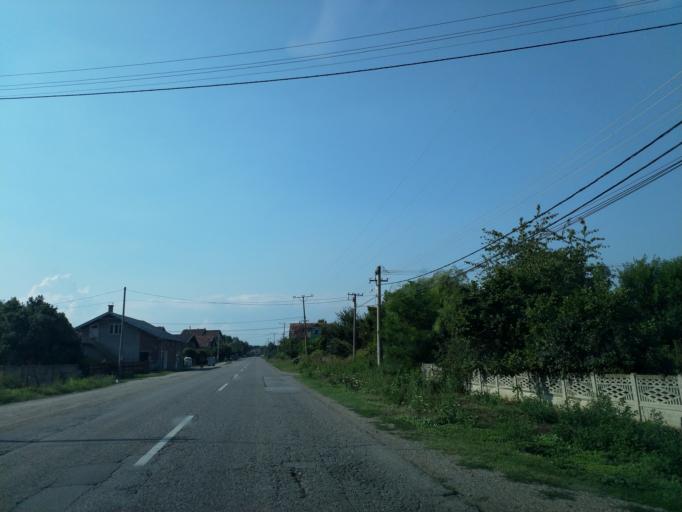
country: RS
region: Central Serbia
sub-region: Rasinski Okrug
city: Cicevac
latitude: 43.7592
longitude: 21.4328
